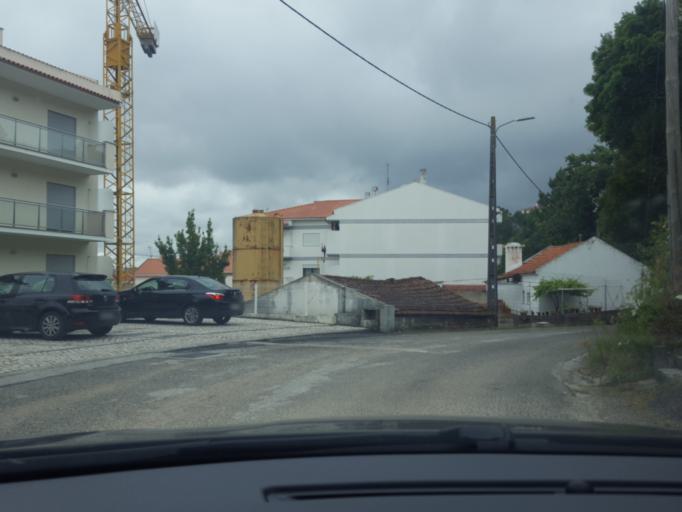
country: PT
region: Leiria
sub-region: Leiria
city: Leiria
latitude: 39.7330
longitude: -8.7919
